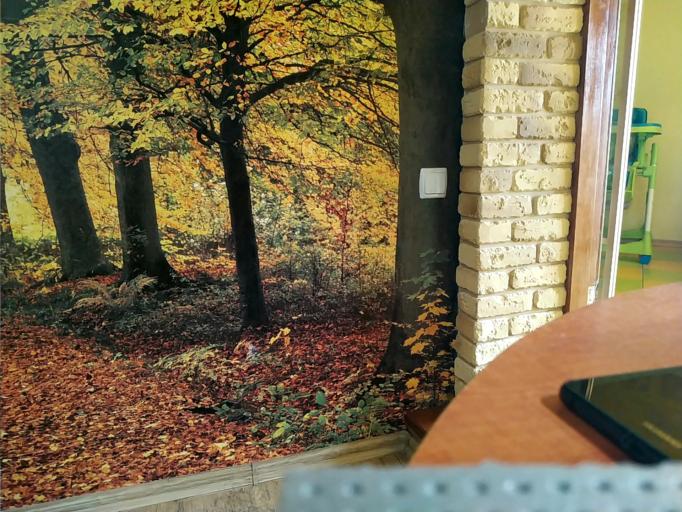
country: RU
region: Tverskaya
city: Kalashnikovo
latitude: 57.2794
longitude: 35.1167
